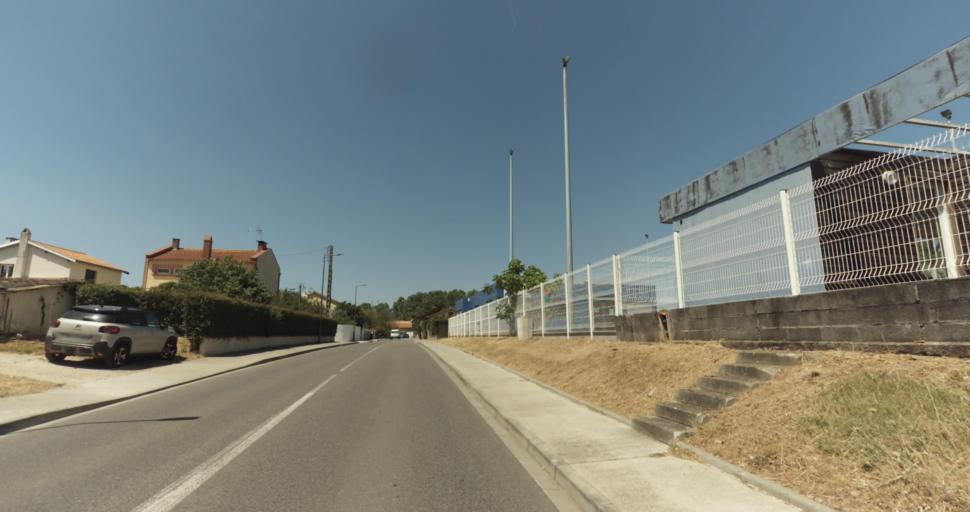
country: FR
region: Midi-Pyrenees
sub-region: Departement de la Haute-Garonne
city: Leguevin
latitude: 43.5972
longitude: 1.2313
